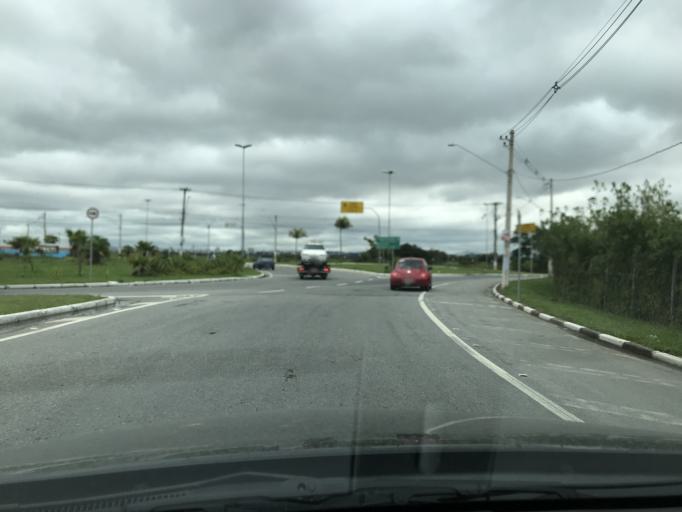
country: BR
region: Sao Paulo
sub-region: Itaquaquecetuba
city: Itaquaquecetuba
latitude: -23.4947
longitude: -46.3251
